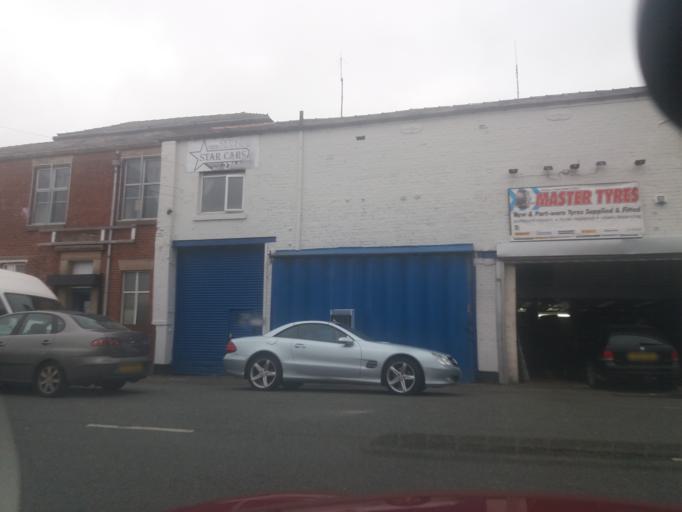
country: GB
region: England
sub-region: Lancashire
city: Chorley
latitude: 53.6544
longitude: -2.6264
